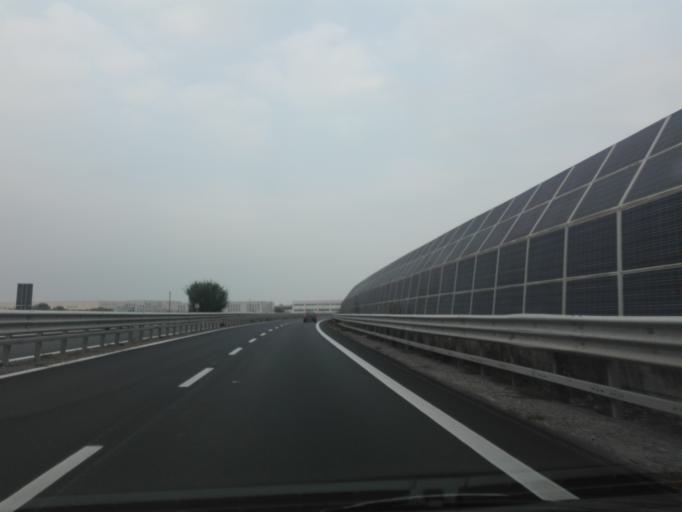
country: IT
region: Veneto
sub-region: Provincia di Verona
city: Vallese
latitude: 45.3235
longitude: 11.0881
